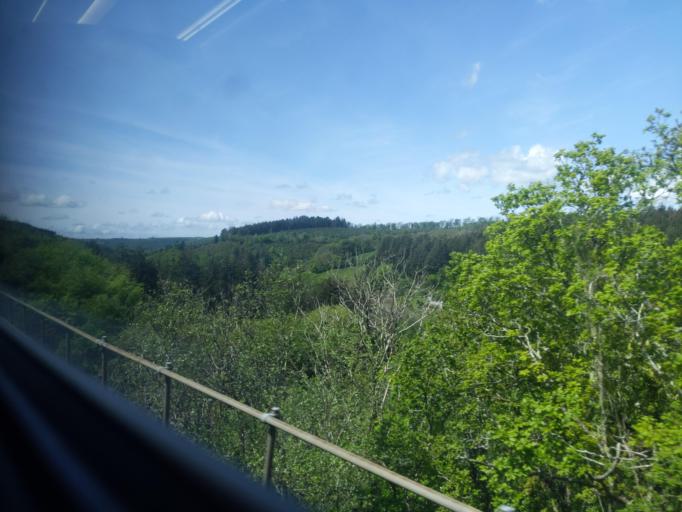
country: GB
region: England
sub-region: Cornwall
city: Liskeard
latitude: 50.4530
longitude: -4.5672
